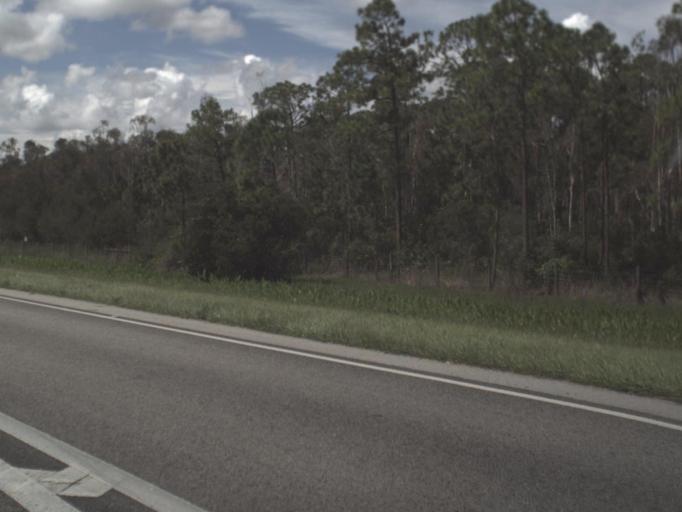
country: US
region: Florida
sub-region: Lee County
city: Fort Myers
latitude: 26.6300
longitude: -81.8046
